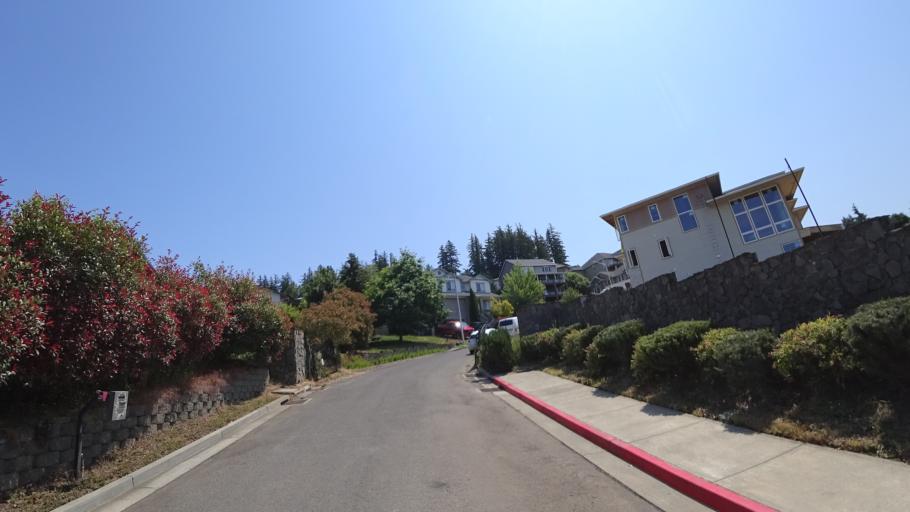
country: US
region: Oregon
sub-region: Multnomah County
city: Lents
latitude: 45.4576
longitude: -122.5683
